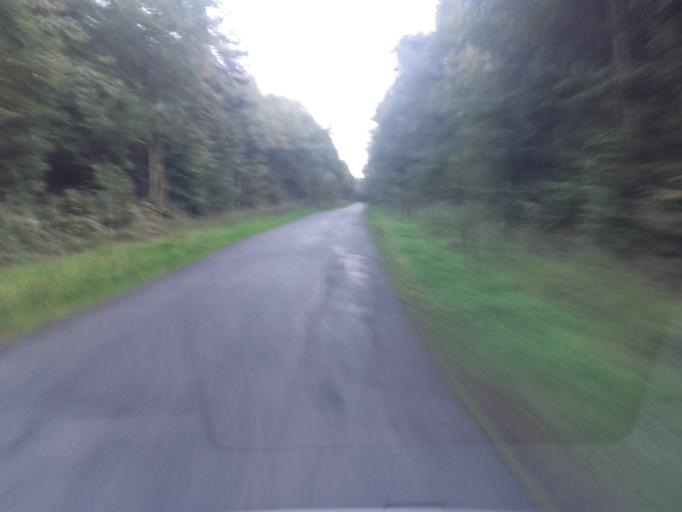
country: FR
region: Brittany
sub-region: Departement des Cotes-d'Armor
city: Plouha
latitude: 48.6562
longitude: -2.9338
